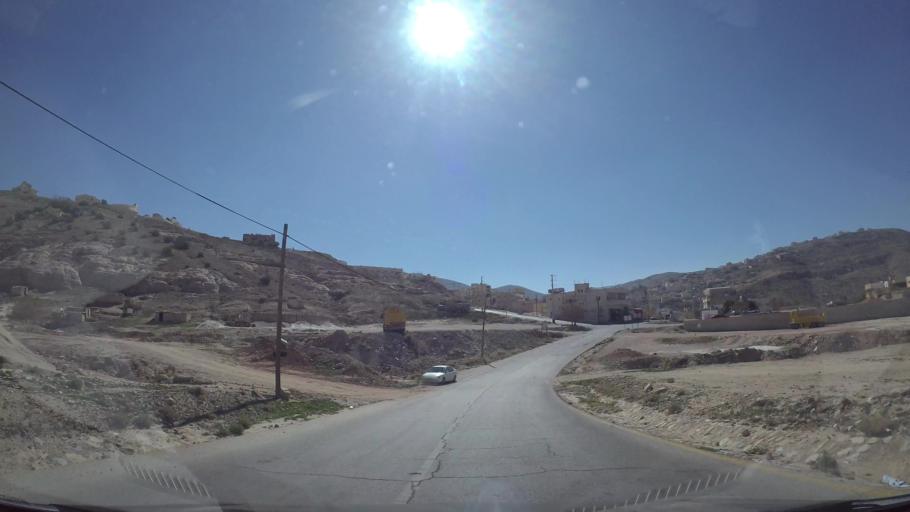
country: JO
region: Ma'an
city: Petra
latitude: 30.3293
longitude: 35.4697
